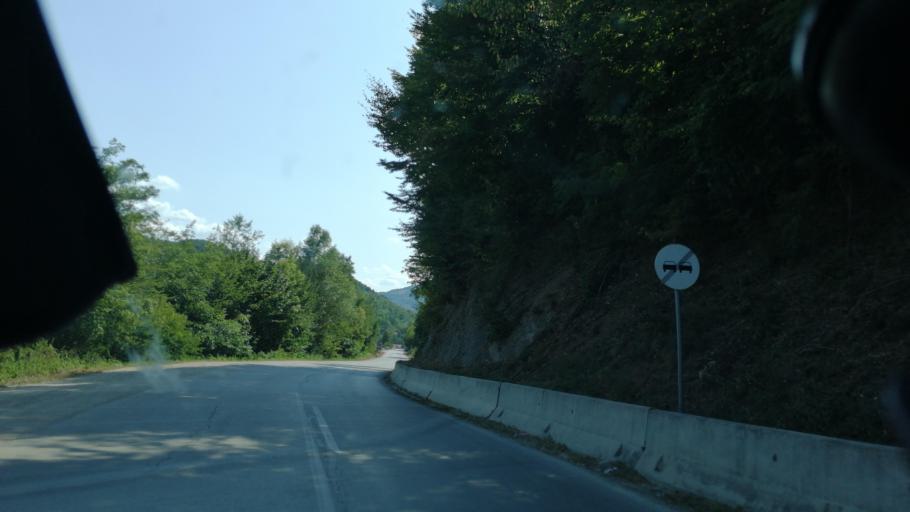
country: RS
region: Central Serbia
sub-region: Moravicki Okrug
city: Ivanjica
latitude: 43.6120
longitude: 20.2359
